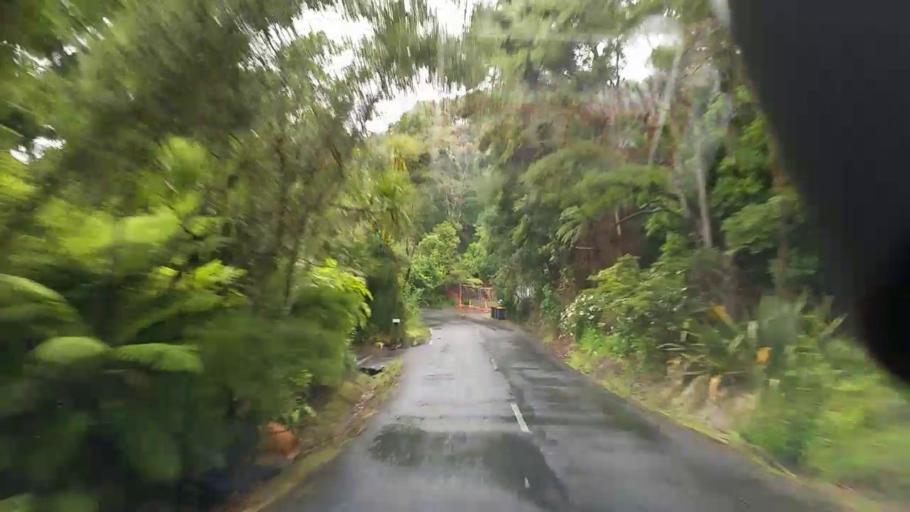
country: NZ
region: Auckland
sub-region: Auckland
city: Waitakere
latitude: -36.9042
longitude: 174.5730
